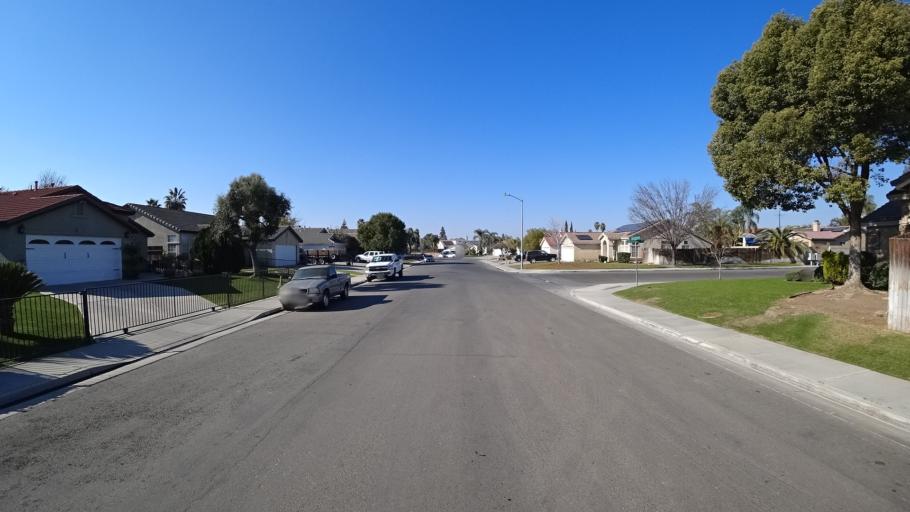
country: US
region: California
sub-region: Kern County
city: Greenfield
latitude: 35.2945
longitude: -119.0436
